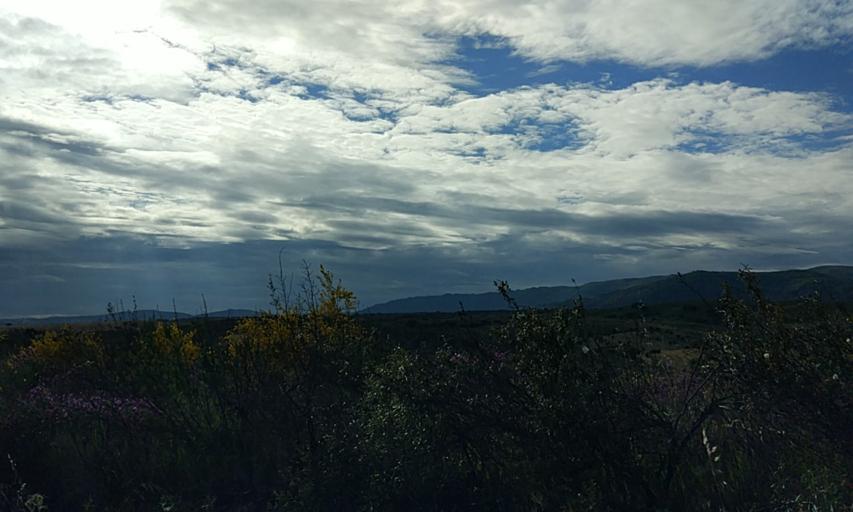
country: ES
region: Extremadura
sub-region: Provincia de Caceres
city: Moraleja
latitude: 40.1087
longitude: -6.6734
